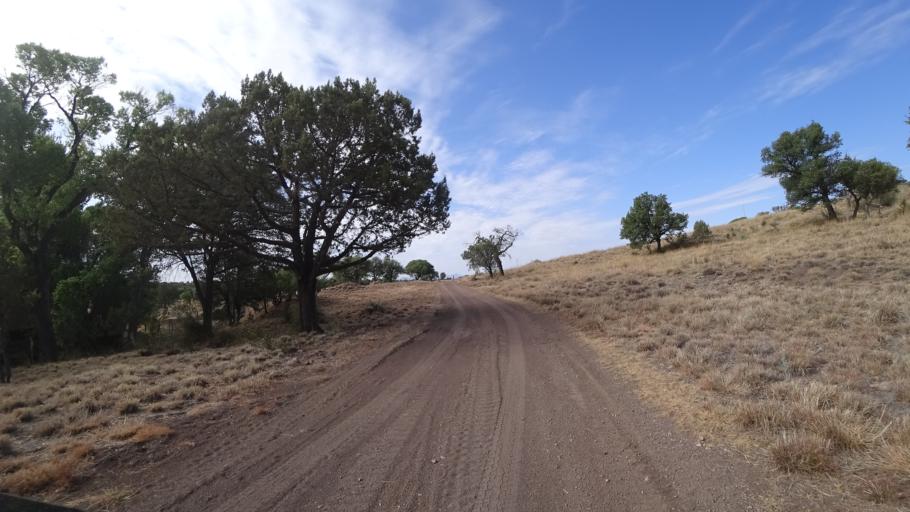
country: MX
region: Sonora
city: Santa Cruz
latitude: 31.4938
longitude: -110.5726
